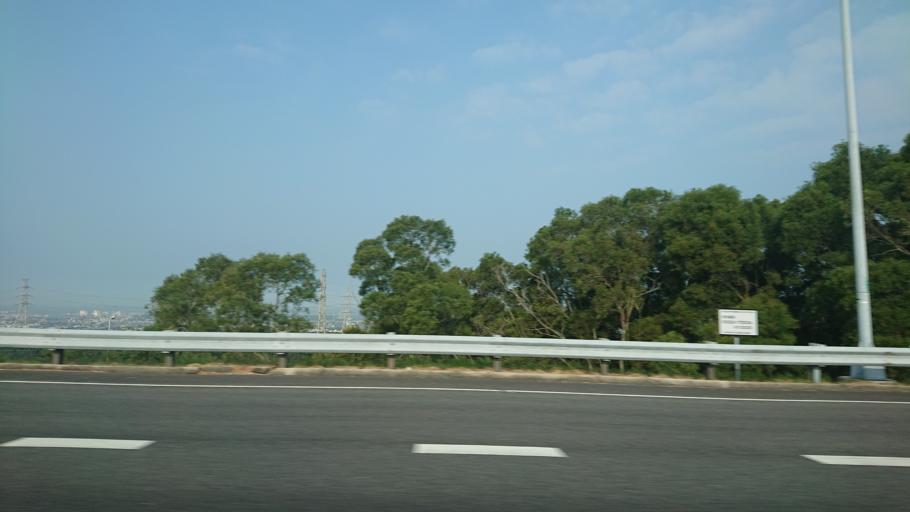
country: TW
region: Taiwan
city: Fengyuan
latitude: 24.2802
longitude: 120.5979
